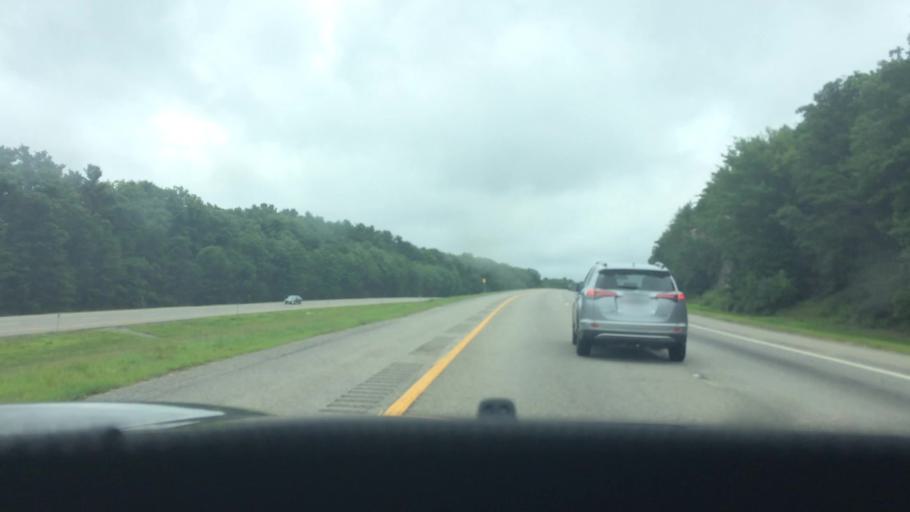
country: US
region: Rhode Island
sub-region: Kent County
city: West Greenwich
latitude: 41.6379
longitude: -71.6269
